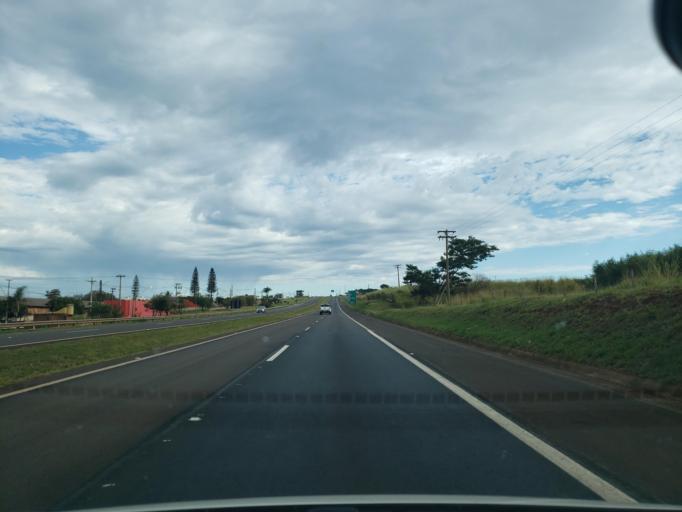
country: BR
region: Sao Paulo
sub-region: Jau
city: Jau
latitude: -22.2598
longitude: -48.5398
